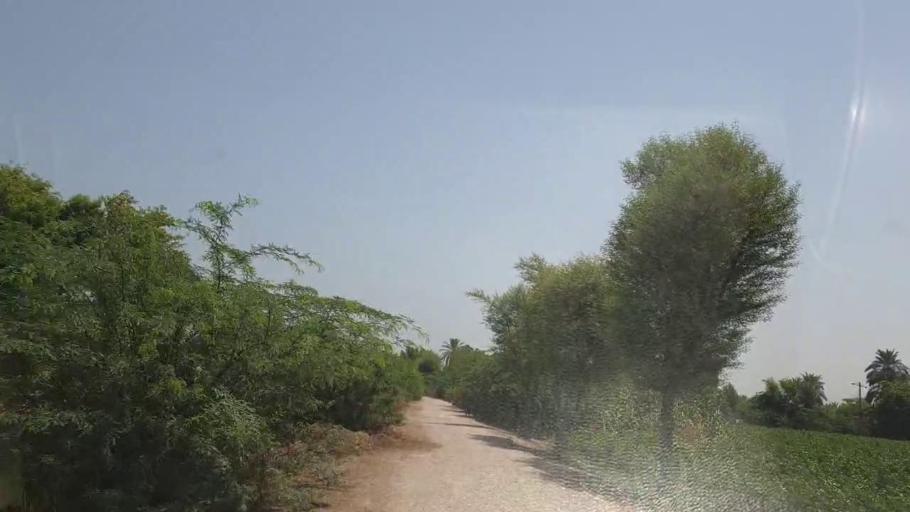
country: PK
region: Sindh
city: Kot Diji
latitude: 27.2839
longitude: 68.6402
